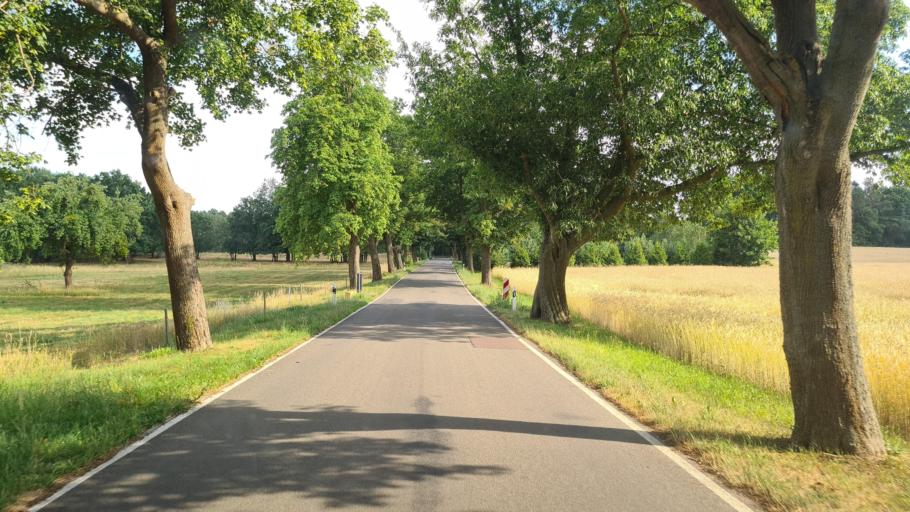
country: DE
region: Saxony-Anhalt
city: Kropstadt
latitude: 51.9381
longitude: 12.7086
